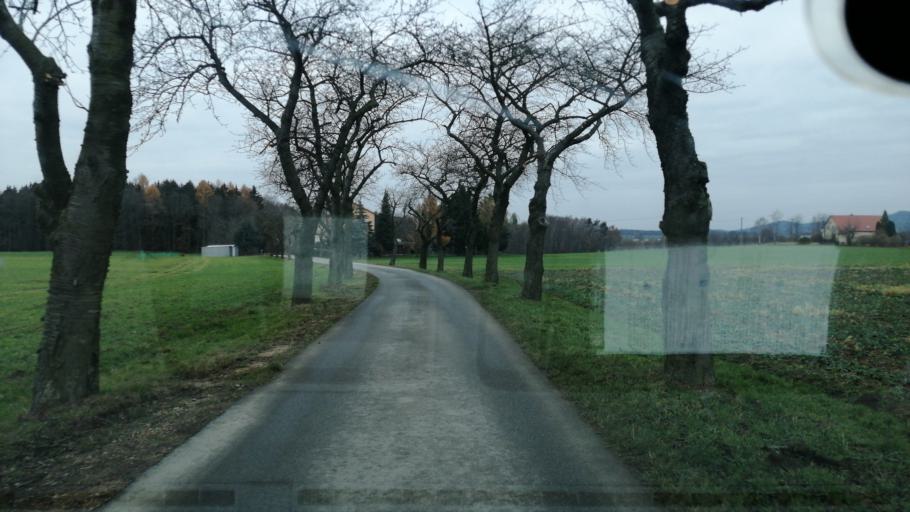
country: DE
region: Saxony
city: Bernstadt
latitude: 51.0545
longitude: 14.7895
